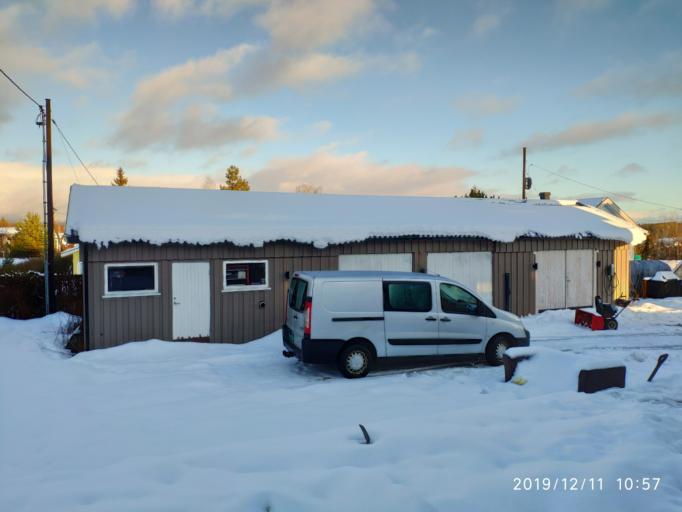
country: NO
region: Akershus
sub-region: Eidsvoll
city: Raholt
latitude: 60.2508
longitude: 11.1998
